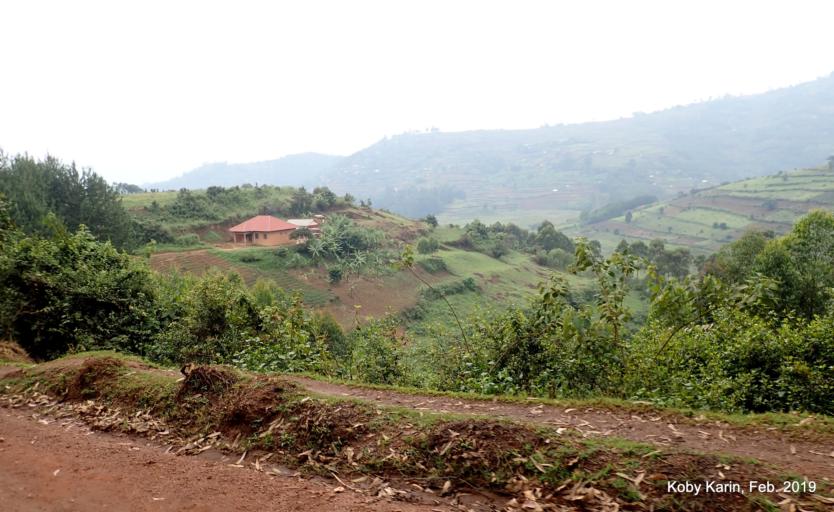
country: UG
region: Western Region
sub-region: Kabale District
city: Kabale
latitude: -1.2617
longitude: 29.9419
